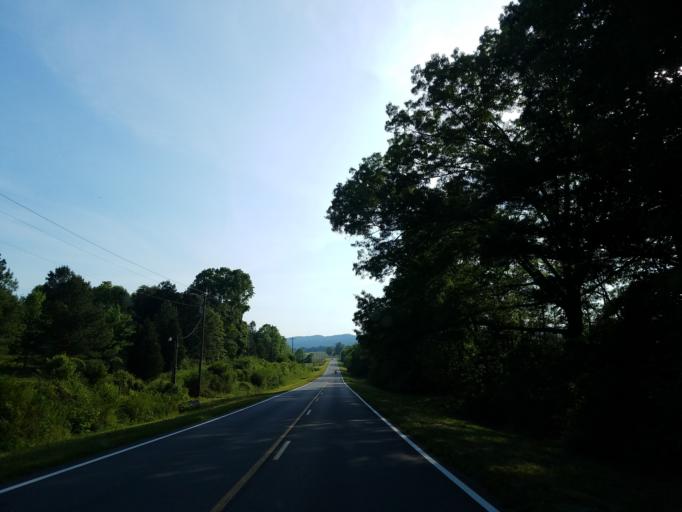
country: US
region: Georgia
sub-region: Chattooga County
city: Trion
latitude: 34.5208
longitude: -85.2215
